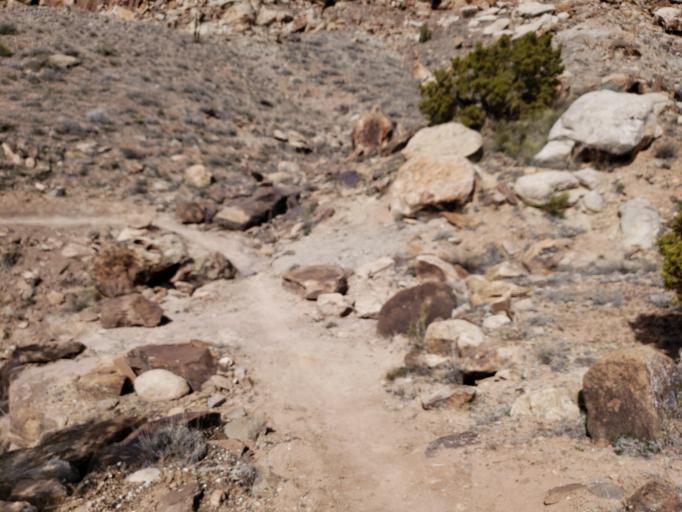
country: US
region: Colorado
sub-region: Mesa County
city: Loma
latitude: 39.1927
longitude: -108.8849
